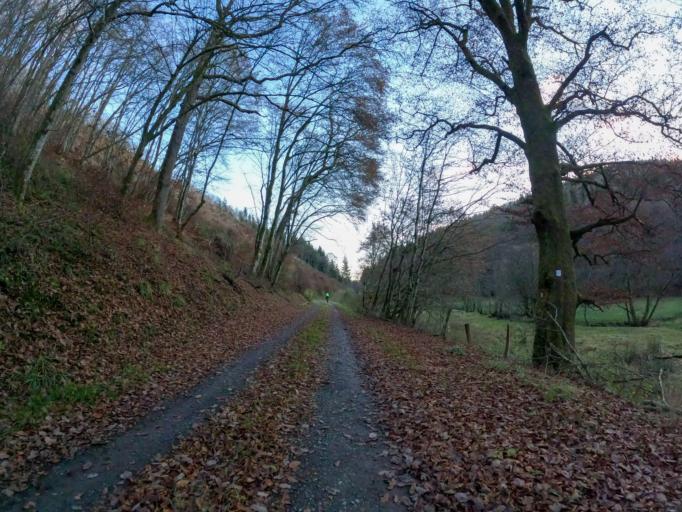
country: LU
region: Diekirch
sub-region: Canton de Wiltz
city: Bavigne
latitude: 49.9386
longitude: 5.8388
